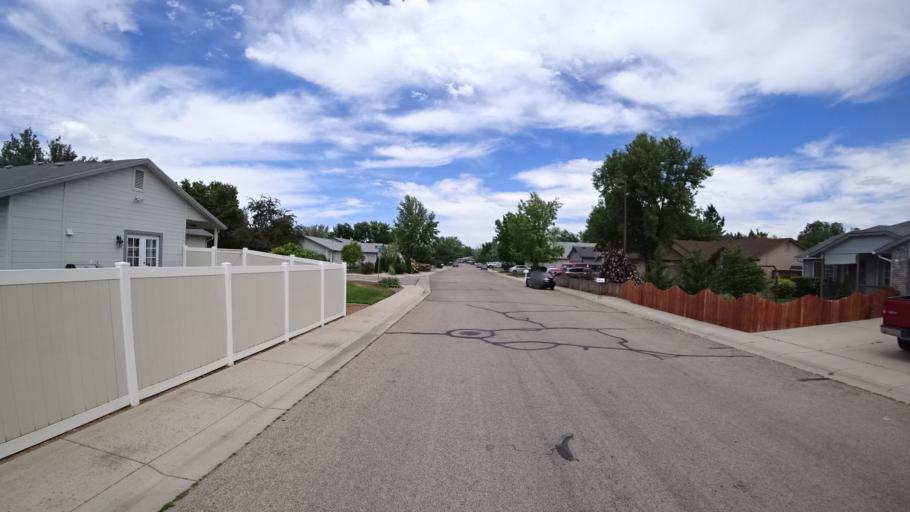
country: US
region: Idaho
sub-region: Ada County
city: Meridian
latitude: 43.6305
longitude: -116.3270
